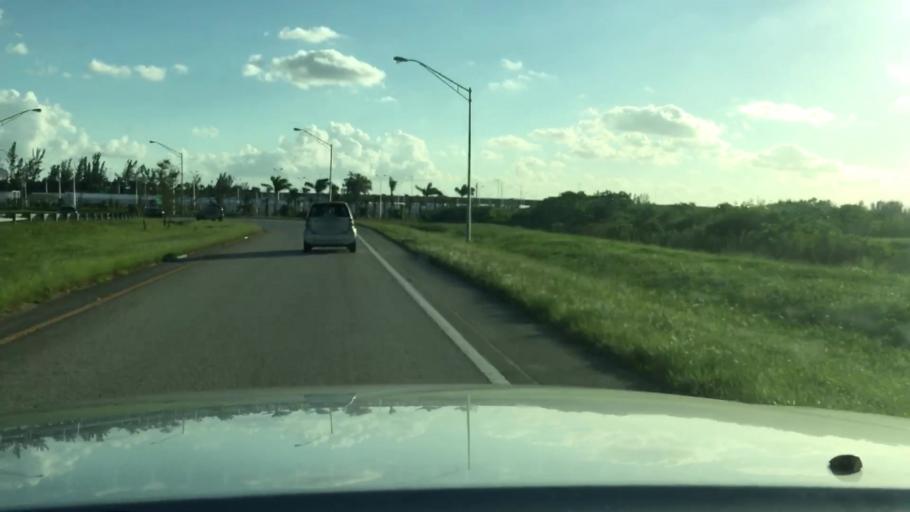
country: US
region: Florida
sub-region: Miami-Dade County
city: Sweetwater
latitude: 25.7865
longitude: -80.3877
